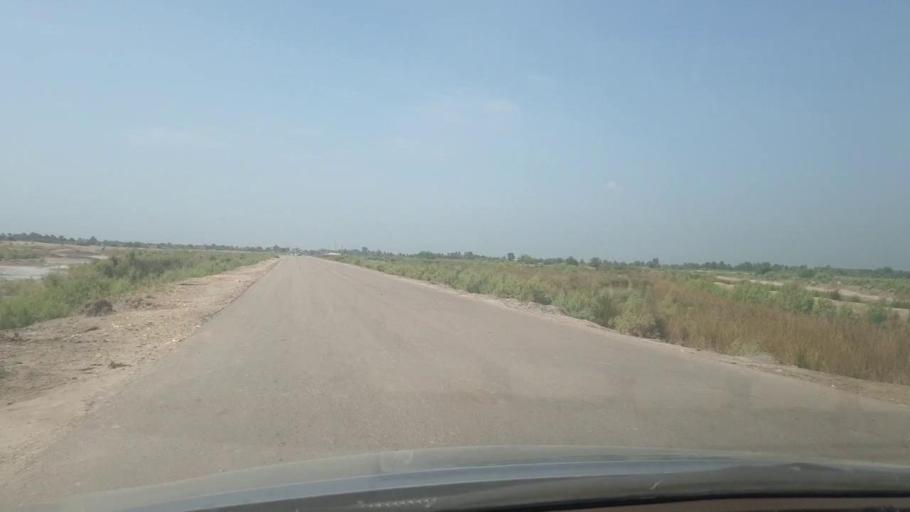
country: PK
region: Sindh
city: Ranipur
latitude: 27.2368
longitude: 68.5712
